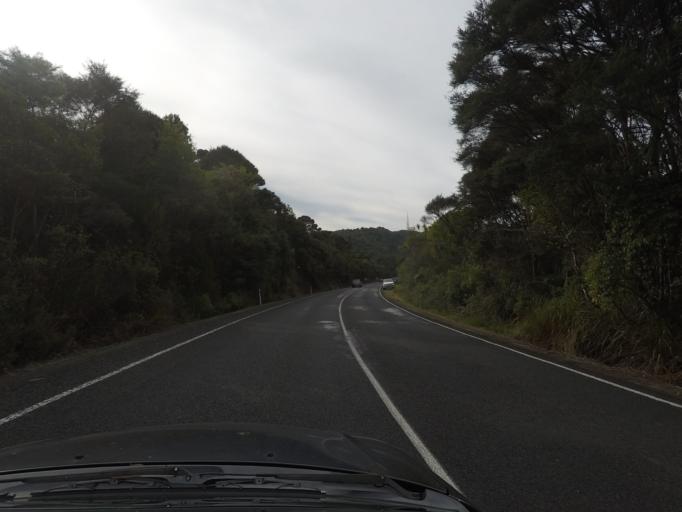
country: NZ
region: Auckland
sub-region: Auckland
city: Titirangi
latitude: -36.9382
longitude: 174.5549
